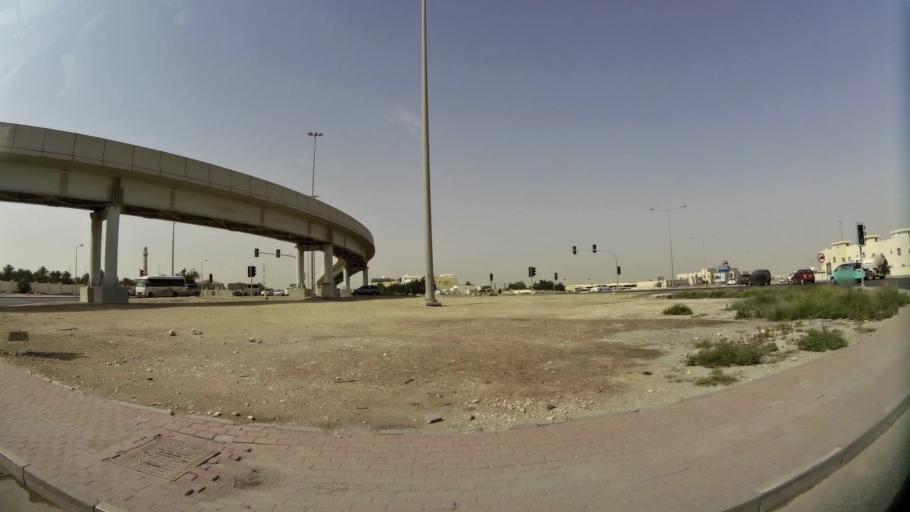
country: QA
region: Baladiyat ad Dawhah
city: Doha
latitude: 25.2378
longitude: 51.5231
